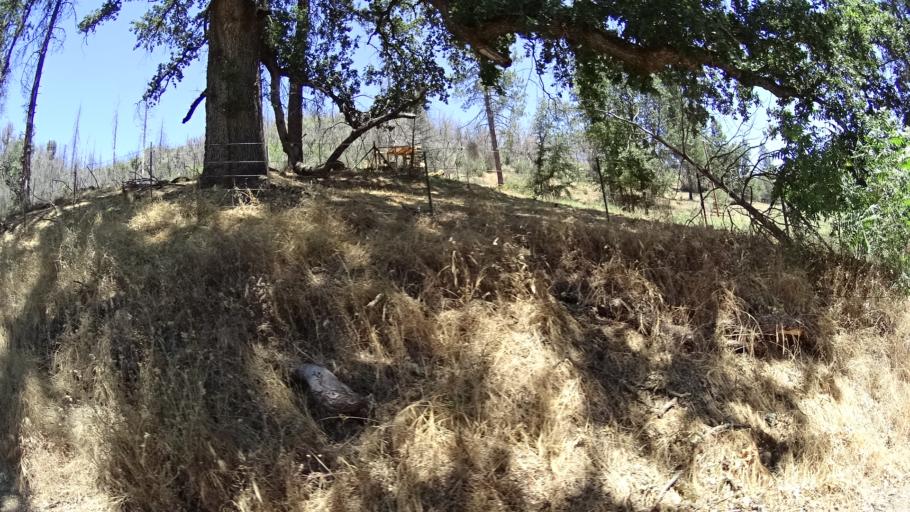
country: US
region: California
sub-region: Calaveras County
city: Mountain Ranch
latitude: 38.2586
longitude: -120.5790
